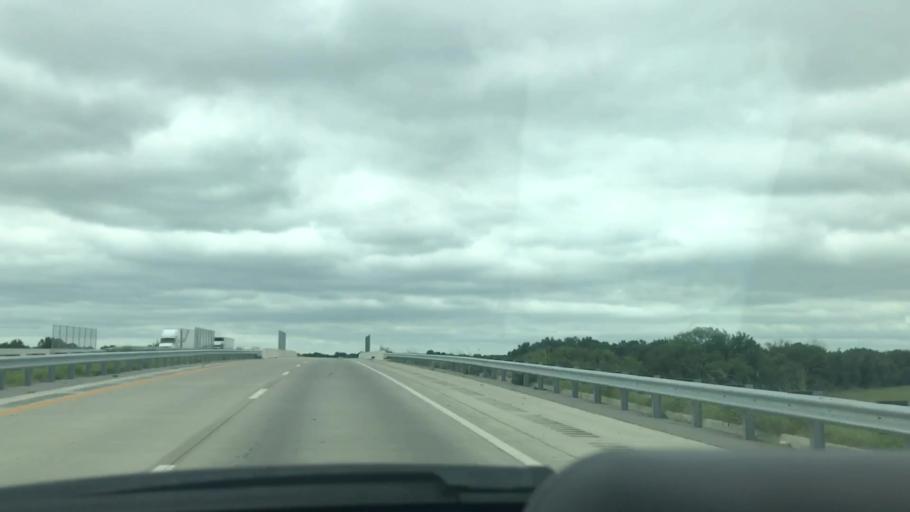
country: US
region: Oklahoma
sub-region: Mayes County
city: Pryor
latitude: 36.3720
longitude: -95.2943
